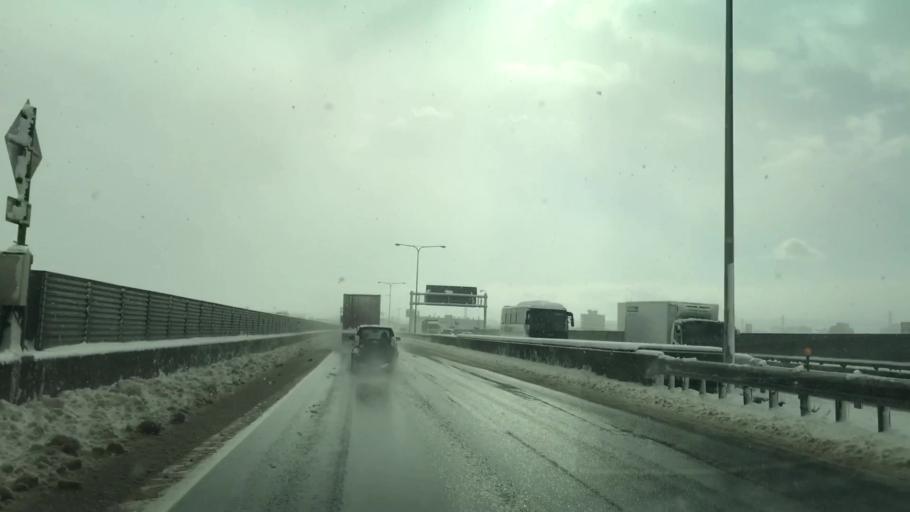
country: JP
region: Hokkaido
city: Sapporo
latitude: 43.0564
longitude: 141.4273
